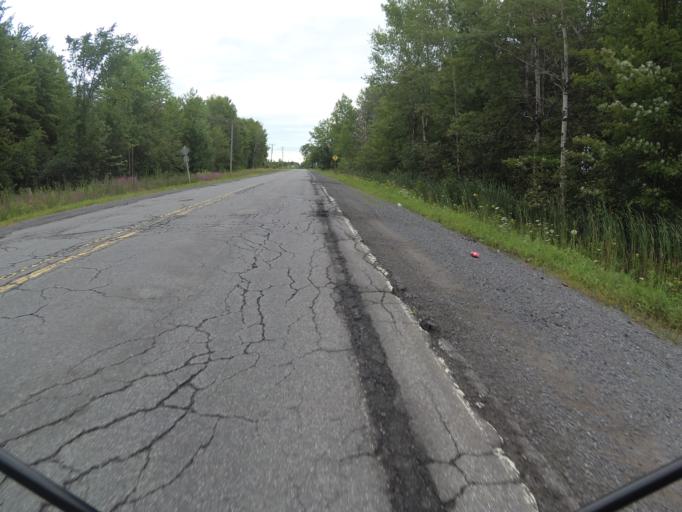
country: CA
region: Ontario
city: Bourget
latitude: 45.3555
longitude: -75.2705
